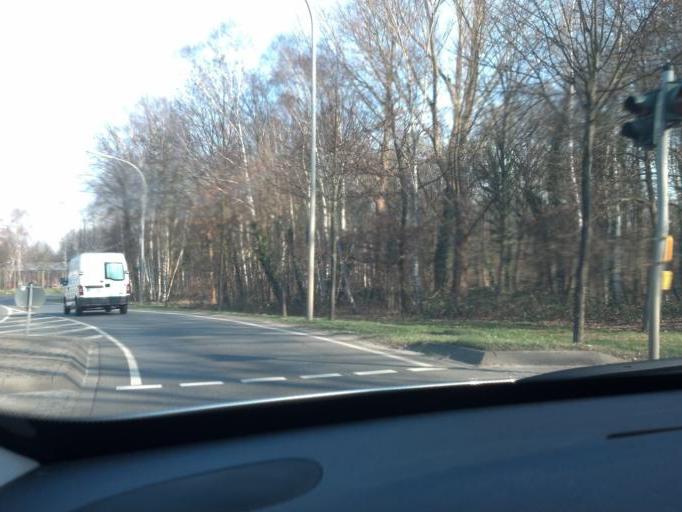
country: DE
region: Lower Saxony
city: Lueneburg
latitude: 53.2577
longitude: 10.4195
